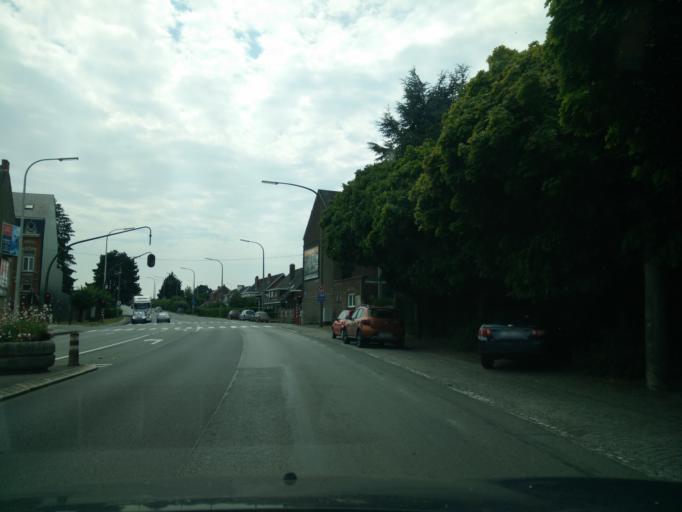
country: BE
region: Wallonia
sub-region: Province du Hainaut
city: Soignies
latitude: 50.5755
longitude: 4.0655
